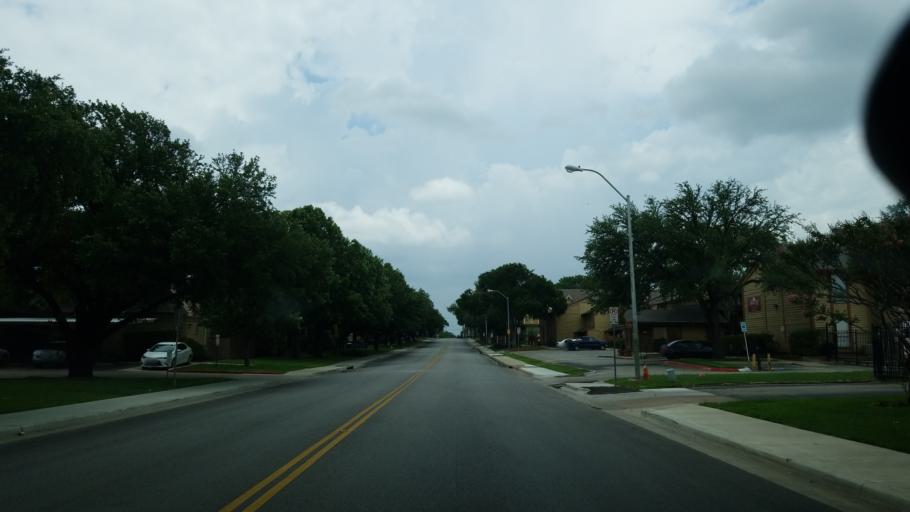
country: US
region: Texas
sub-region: Dallas County
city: Farmers Branch
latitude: 32.8758
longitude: -96.8750
